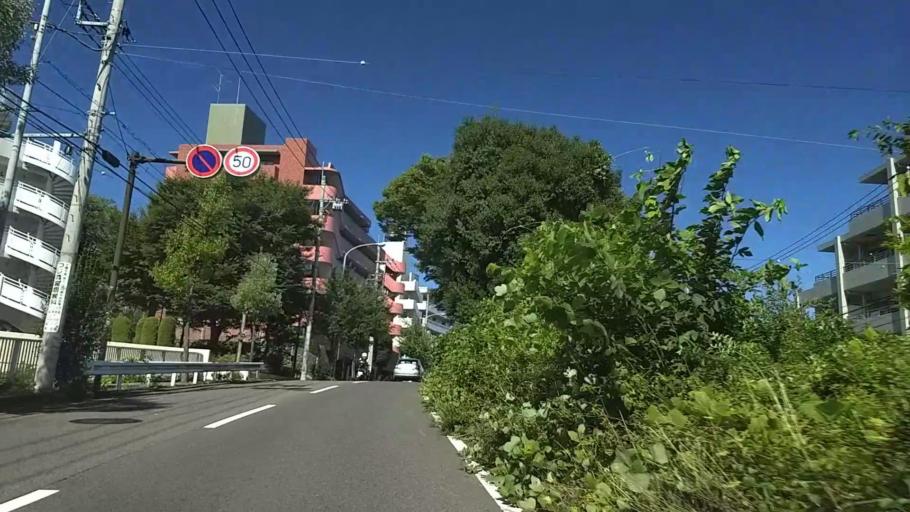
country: JP
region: Tokyo
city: Chofugaoka
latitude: 35.5714
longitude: 139.5526
